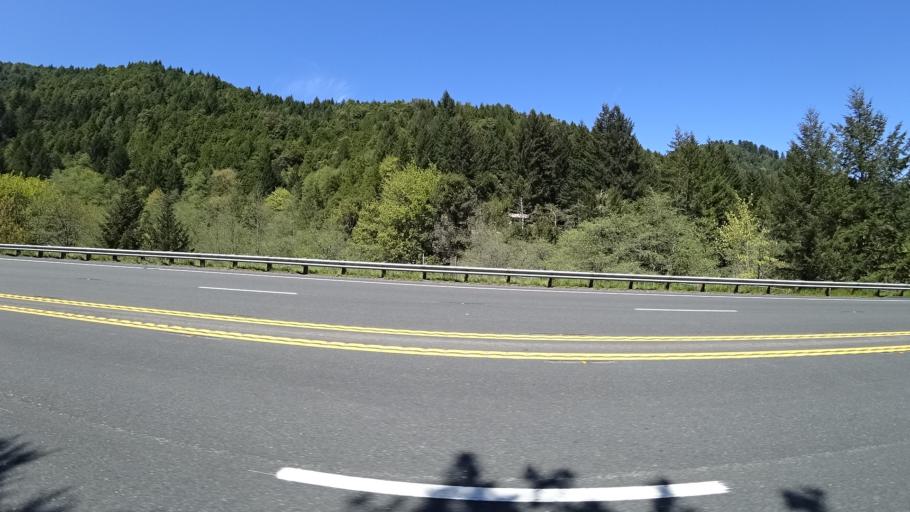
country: US
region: California
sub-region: Humboldt County
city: Willow Creek
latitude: 40.9154
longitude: -123.7025
